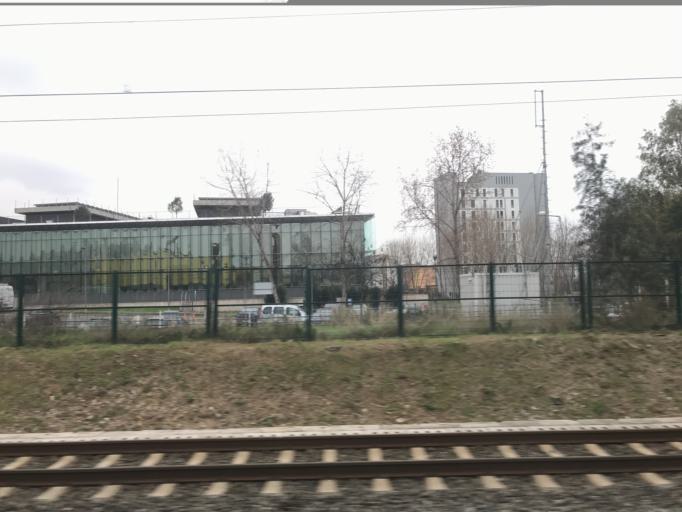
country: TR
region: Kocaeli
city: Darica
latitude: 40.8069
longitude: 29.3675
